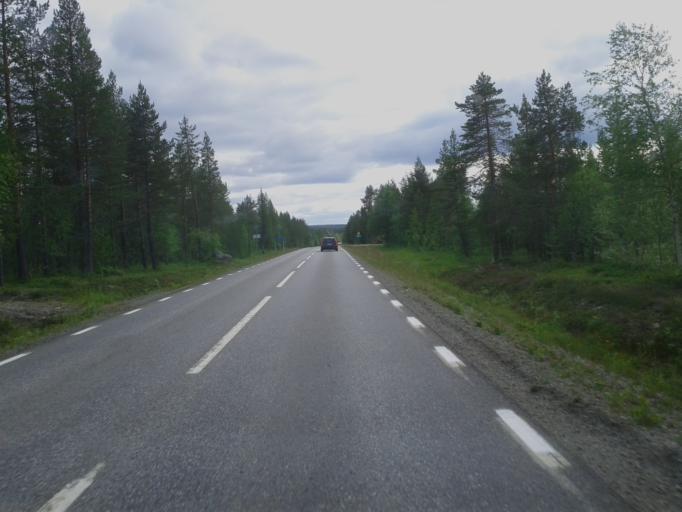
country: SE
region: Vaesterbotten
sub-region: Sorsele Kommun
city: Sorsele
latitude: 65.2275
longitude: 17.6509
